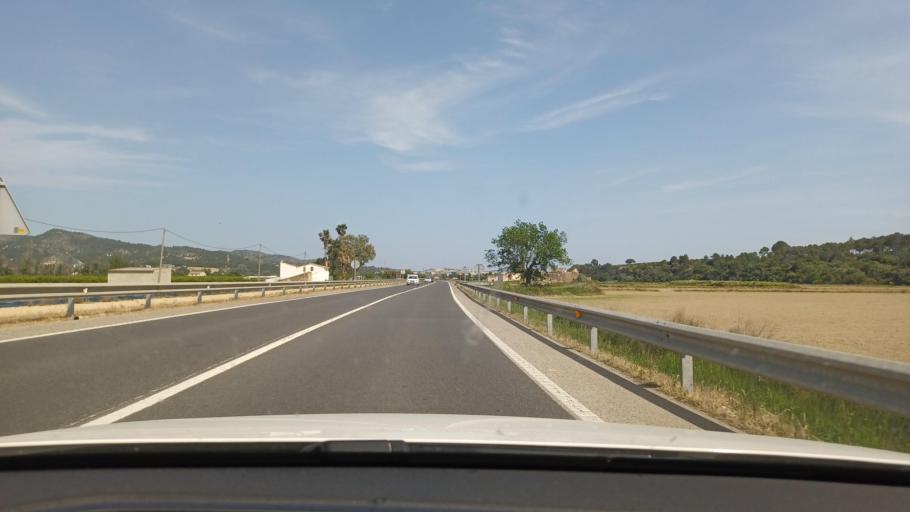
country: ES
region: Catalonia
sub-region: Provincia de Tarragona
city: Tortosa
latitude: 40.7763
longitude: 0.5149
